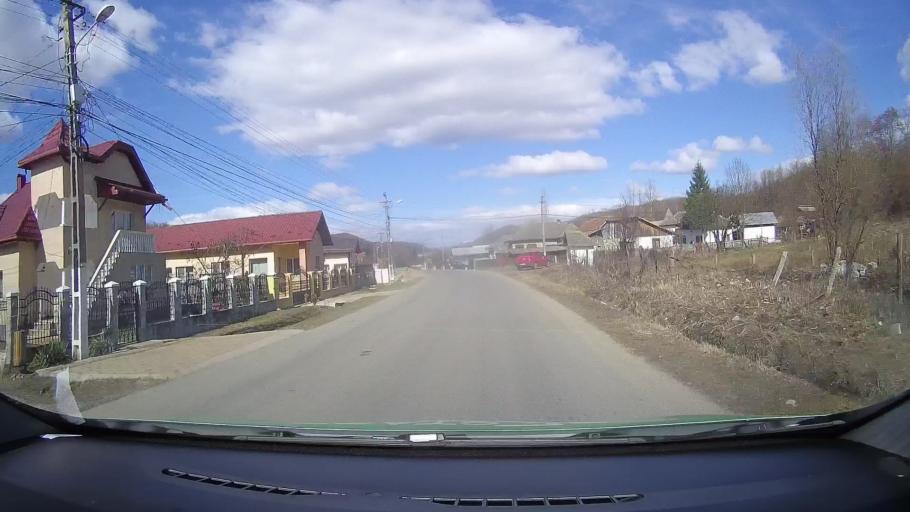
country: RO
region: Dambovita
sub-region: Comuna Vulcana-Pandele
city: Gura Vulcanei
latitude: 45.0343
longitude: 25.3930
